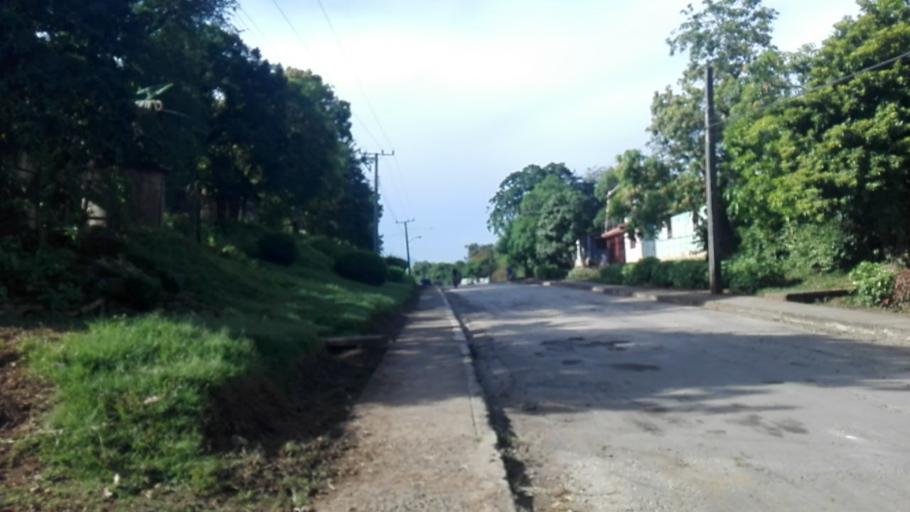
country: CU
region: Granma
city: Bartolome Maso
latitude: 20.1590
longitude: -76.9490
